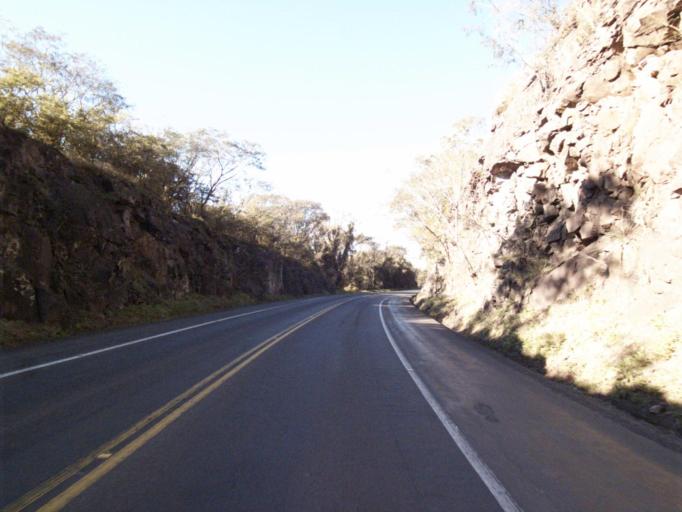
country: BR
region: Rio Grande do Sul
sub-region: Frederico Westphalen
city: Frederico Westphalen
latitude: -26.8055
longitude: -53.4414
